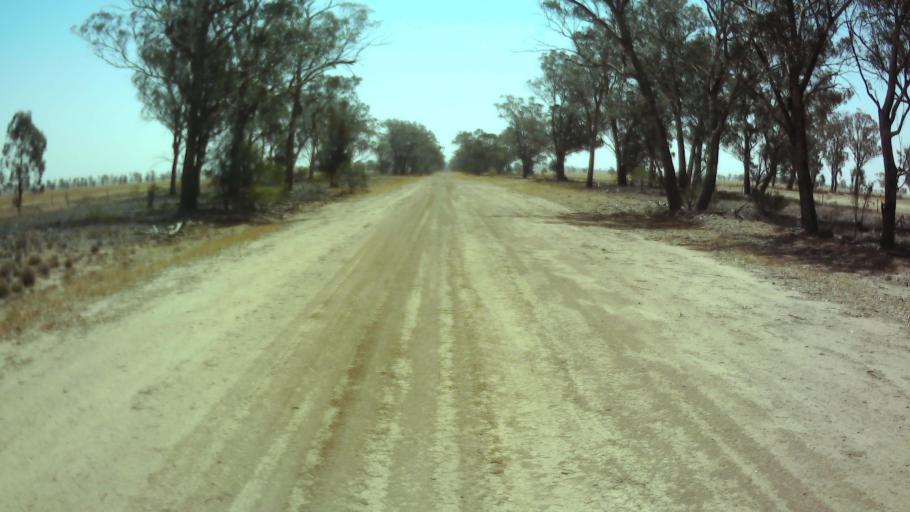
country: AU
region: New South Wales
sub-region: Weddin
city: Grenfell
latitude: -33.9342
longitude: 147.8037
